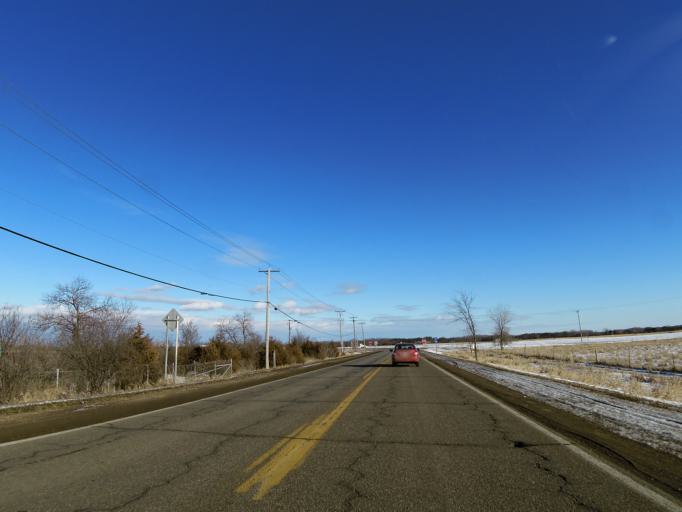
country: US
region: Minnesota
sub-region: Washington County
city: Lakeland
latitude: 44.9532
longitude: -92.7989
